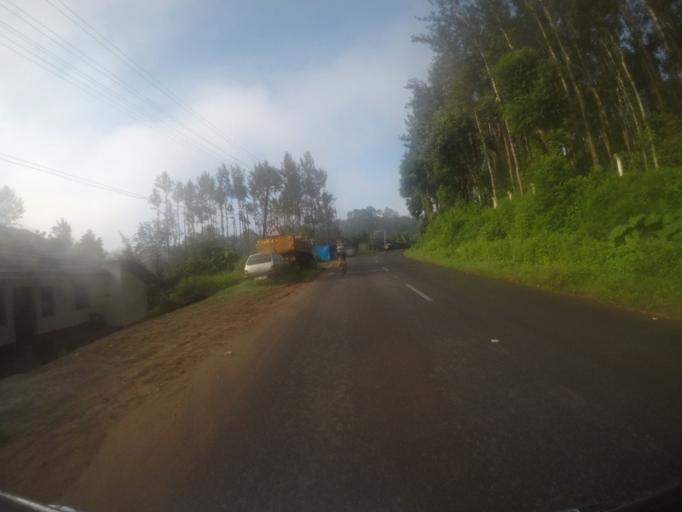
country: IN
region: Karnataka
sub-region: Kodagu
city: Suntikoppa
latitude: 12.4402
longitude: 75.8108
